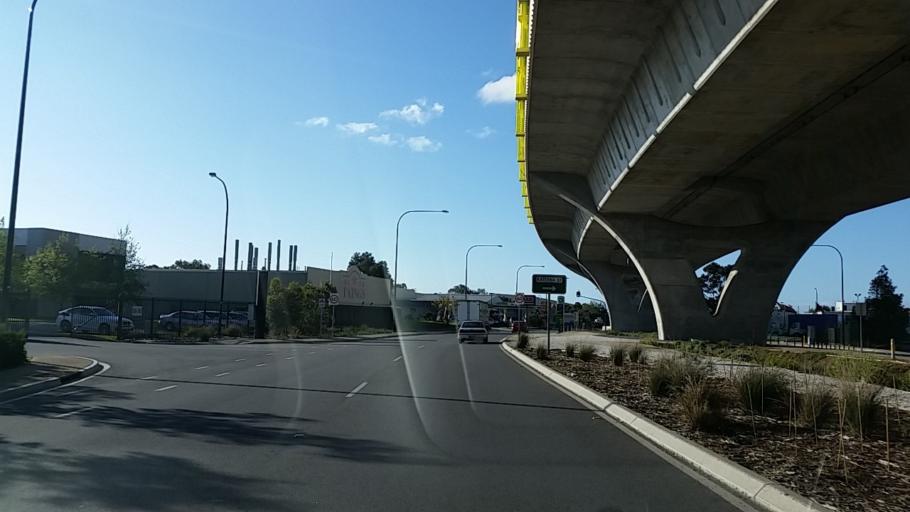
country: AU
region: South Australia
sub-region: Charles Sturt
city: Woodville North
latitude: -34.8578
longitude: 138.5653
